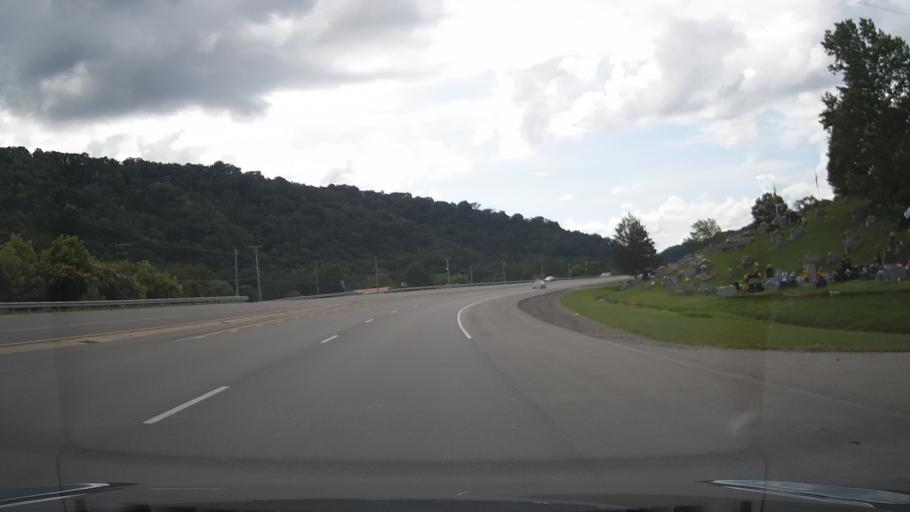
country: US
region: Kentucky
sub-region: Floyd County
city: Prestonsburg
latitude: 37.5935
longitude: -82.6761
